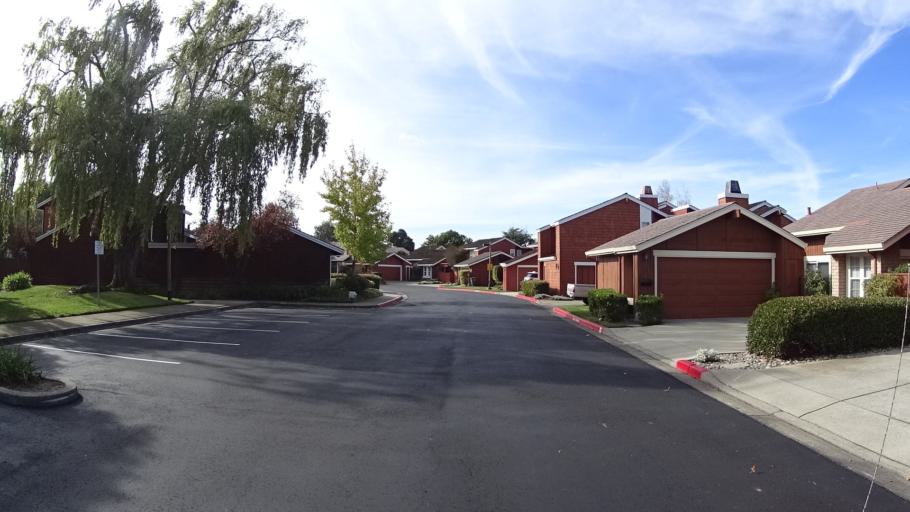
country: US
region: California
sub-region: San Mateo County
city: Foster City
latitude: 37.5464
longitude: -122.2582
